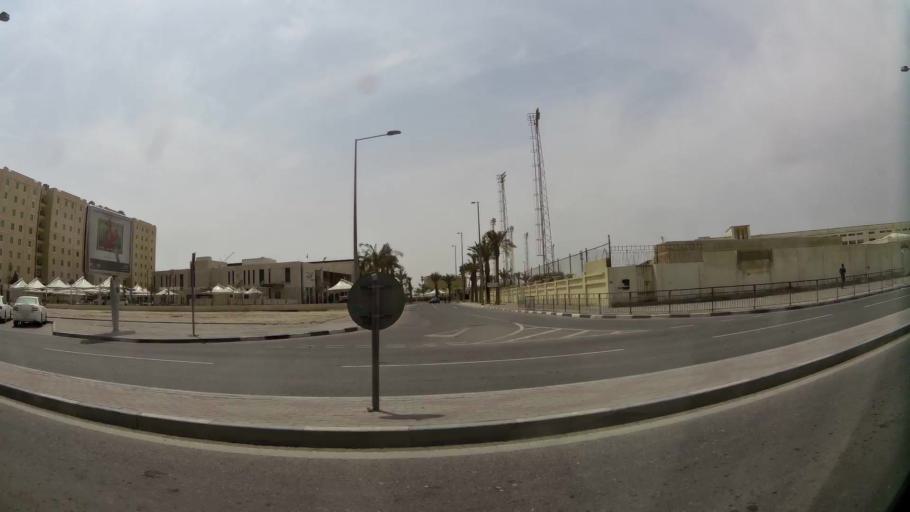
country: QA
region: Baladiyat ad Dawhah
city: Doha
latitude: 25.2764
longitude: 51.5201
